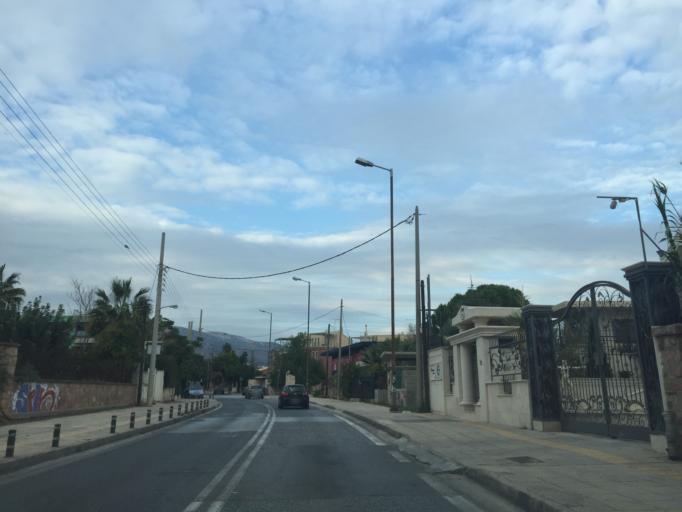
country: GR
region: Attica
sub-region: Nomarchia Anatolikis Attikis
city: Vari
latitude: 37.8239
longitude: 23.8042
